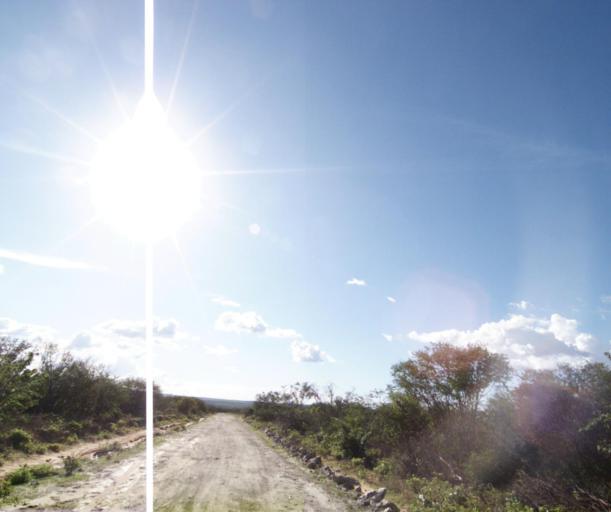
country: BR
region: Bahia
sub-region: Tanhacu
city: Tanhacu
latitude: -14.1876
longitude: -40.9822
